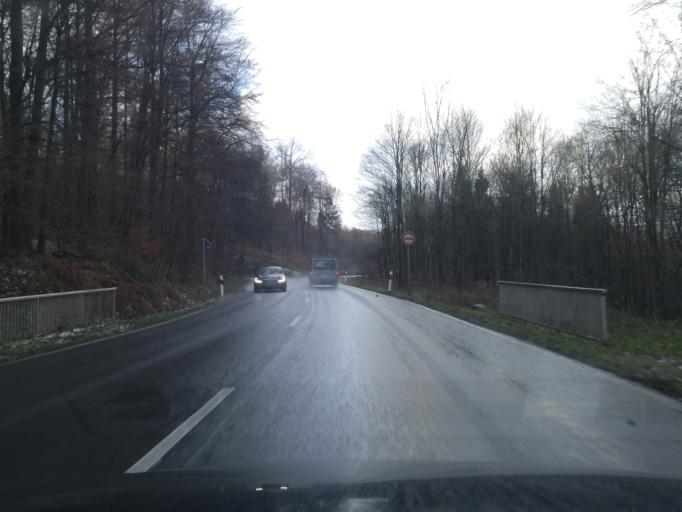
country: DE
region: Lower Saxony
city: Hannoversch Munden
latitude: 51.3848
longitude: 9.6267
